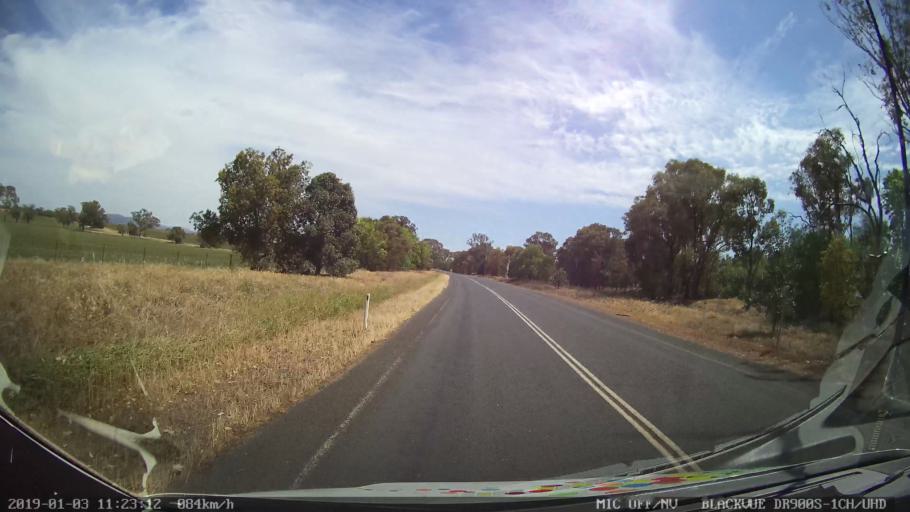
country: AU
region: New South Wales
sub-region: Weddin
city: Grenfell
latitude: -34.0660
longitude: 148.2439
